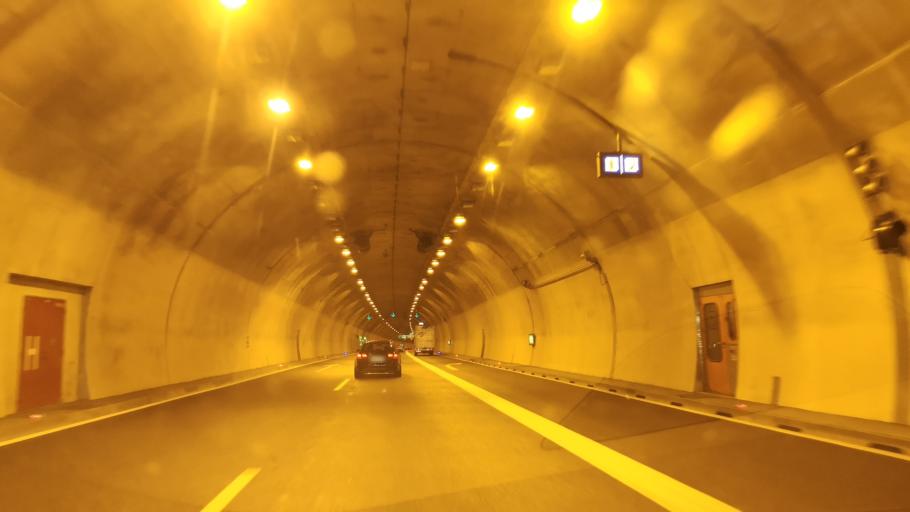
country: SI
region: Ljubljana
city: Ljubljana
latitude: 46.0892
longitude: 14.4607
